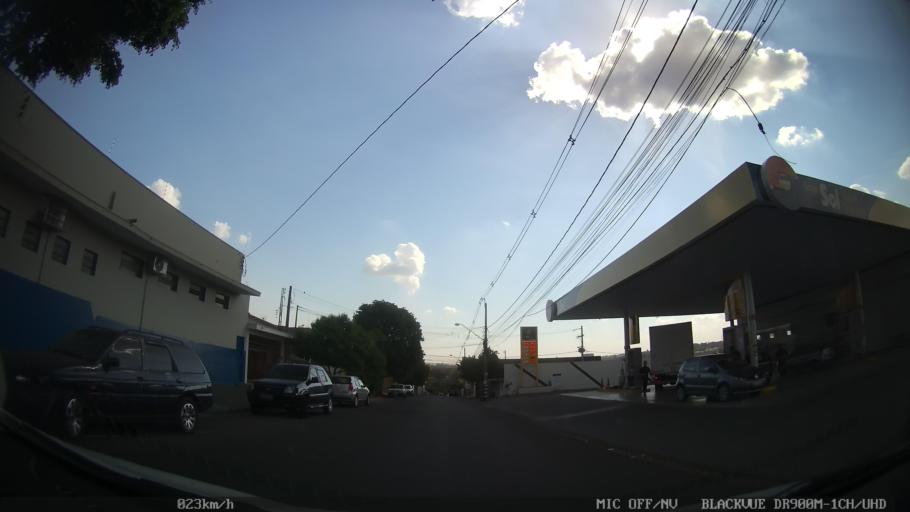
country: BR
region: Sao Paulo
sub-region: Ribeirao Preto
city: Ribeirao Preto
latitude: -21.1821
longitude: -47.8366
